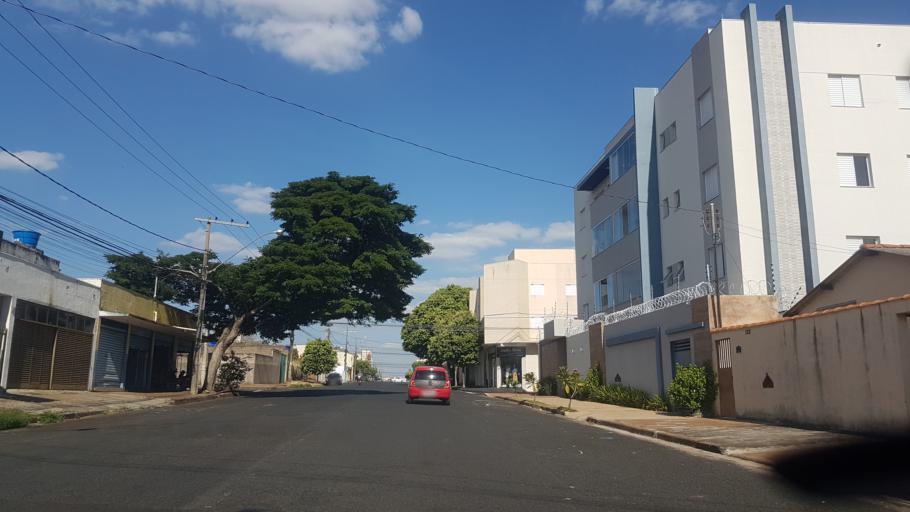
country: BR
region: Minas Gerais
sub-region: Uberlandia
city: Uberlandia
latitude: -18.9025
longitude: -48.2567
